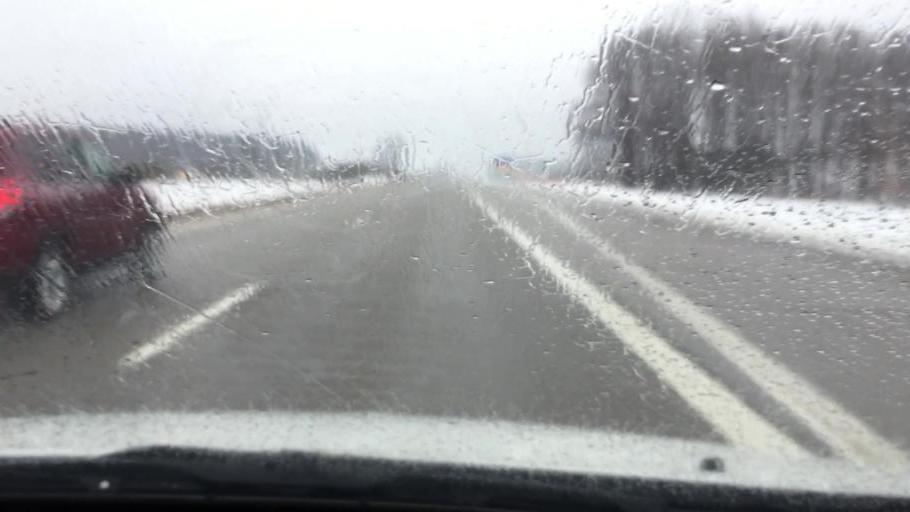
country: US
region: Michigan
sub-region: Wexford County
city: Cadillac
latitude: 44.1269
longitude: -85.4690
